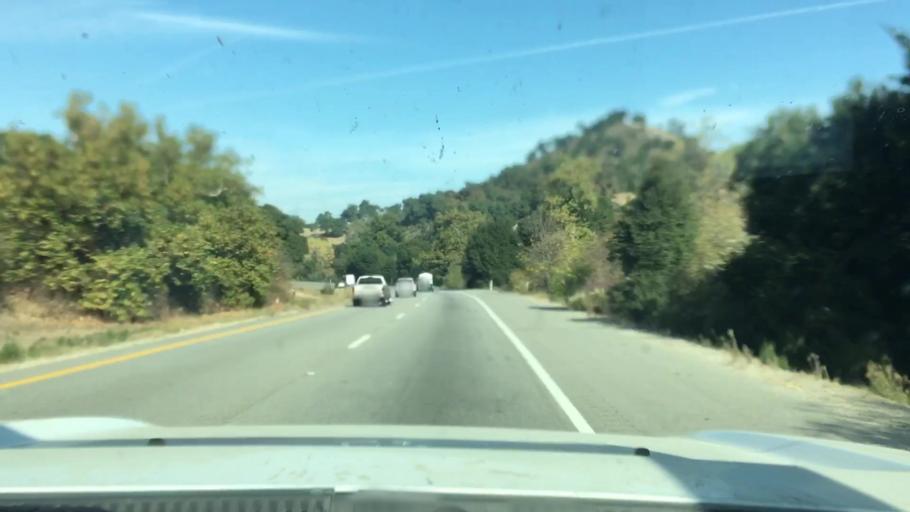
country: US
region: California
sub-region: San Luis Obispo County
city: Santa Margarita
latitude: 35.3628
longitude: -120.6376
